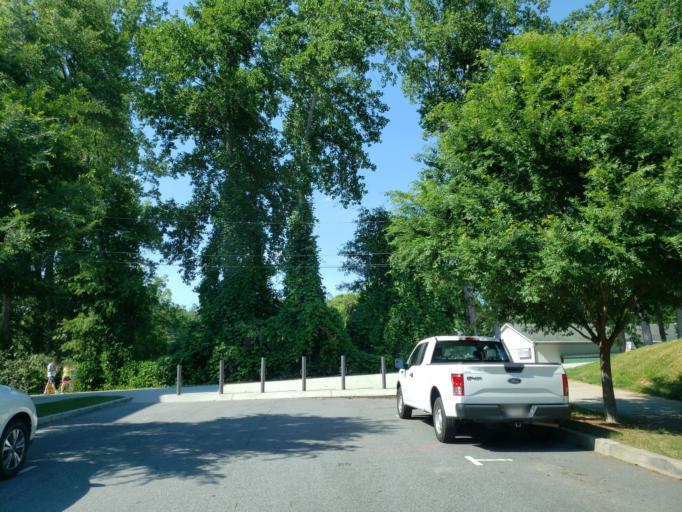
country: US
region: Georgia
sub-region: Cherokee County
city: Woodstock
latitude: 34.1004
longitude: -84.5225
